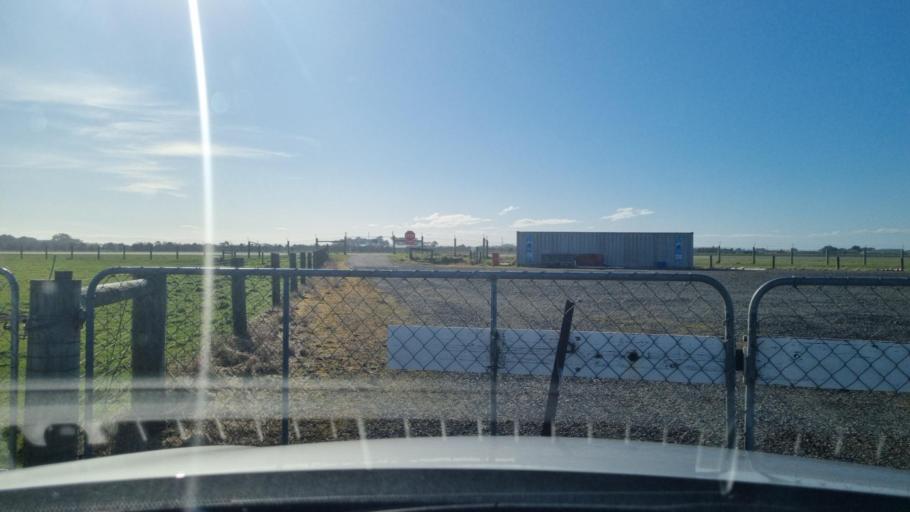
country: NZ
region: Southland
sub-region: Invercargill City
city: Invercargill
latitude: -46.4185
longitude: 168.3069
